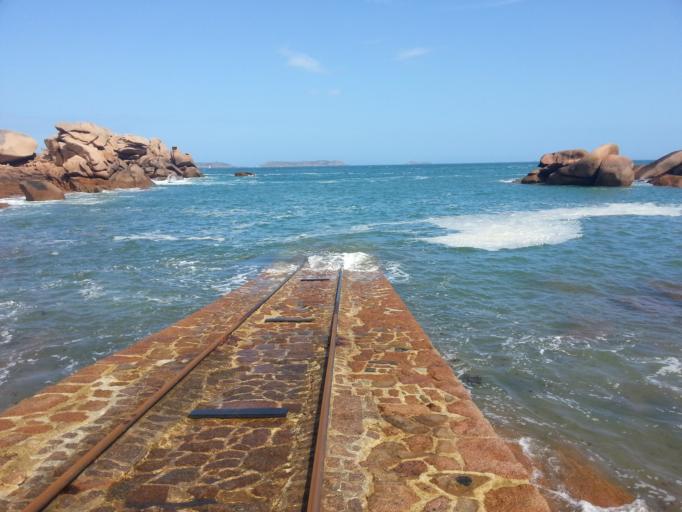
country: FR
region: Brittany
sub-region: Departement des Cotes-d'Armor
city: Tregastel
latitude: 48.8368
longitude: -3.4816
